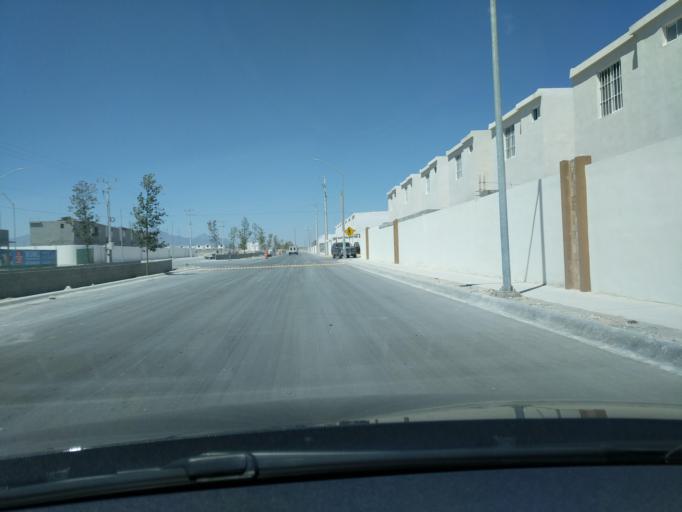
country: MX
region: Nuevo Leon
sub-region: Apodaca
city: Artemio Trevino
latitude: 25.8430
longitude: -100.1393
